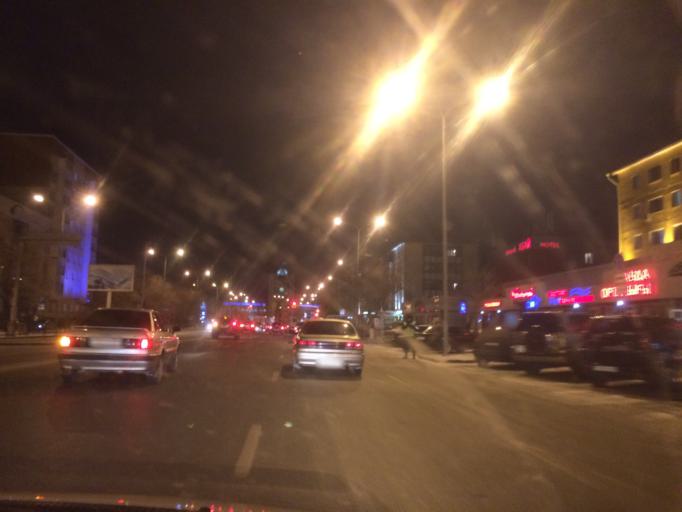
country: KZ
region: Astana Qalasy
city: Astana
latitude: 51.1921
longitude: 71.4071
